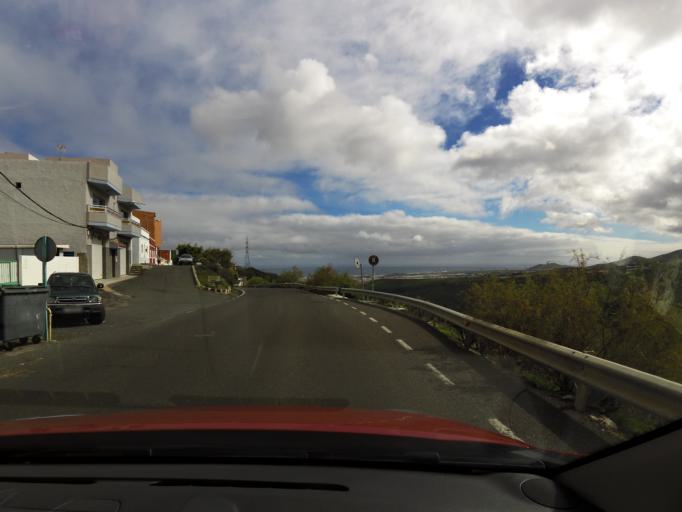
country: ES
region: Canary Islands
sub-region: Provincia de Las Palmas
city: Telde
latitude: 28.0165
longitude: -15.4510
